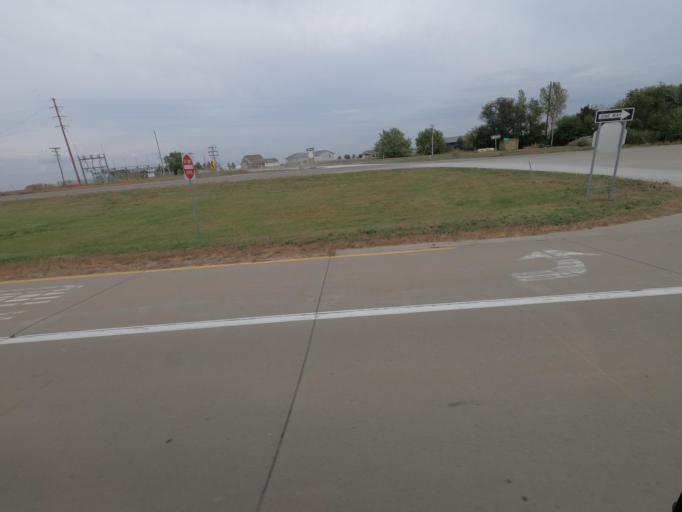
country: US
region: Iowa
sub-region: Marion County
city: Pella
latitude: 41.4393
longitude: -93.0056
